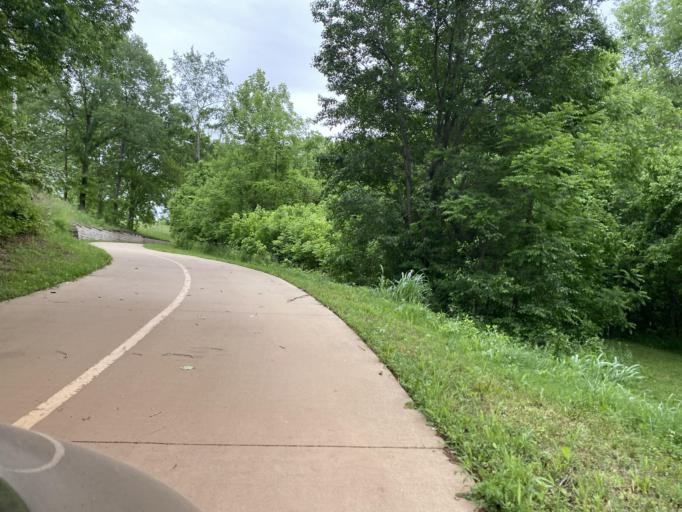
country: US
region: Arkansas
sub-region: Benton County
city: Bentonville
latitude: 36.3709
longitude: -94.2379
